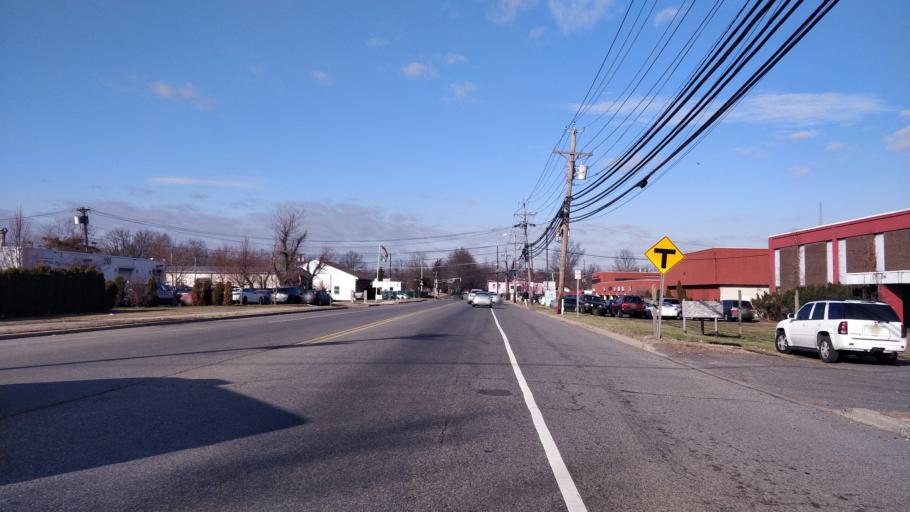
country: US
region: New Jersey
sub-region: Middlesex County
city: South Plainfield
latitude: 40.5782
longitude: -74.4311
